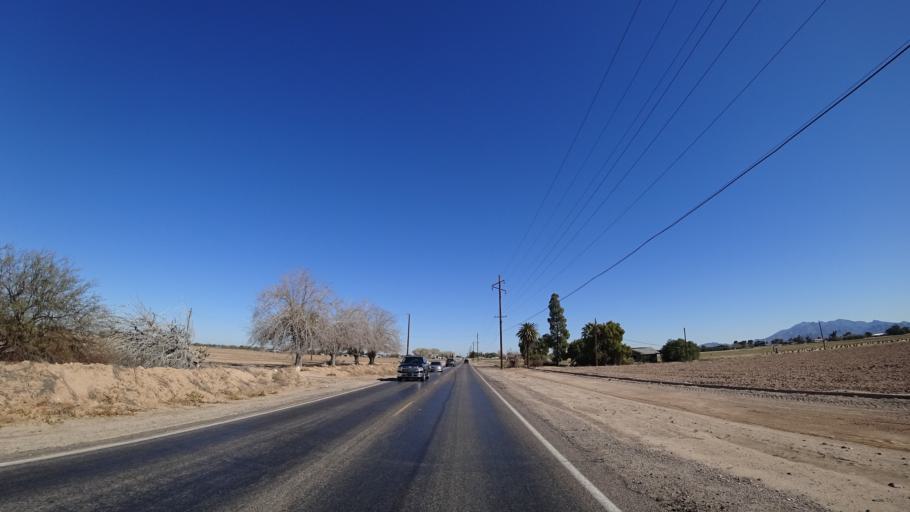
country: US
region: Arizona
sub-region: Maricopa County
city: Goodyear
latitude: 33.4357
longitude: -112.4538
